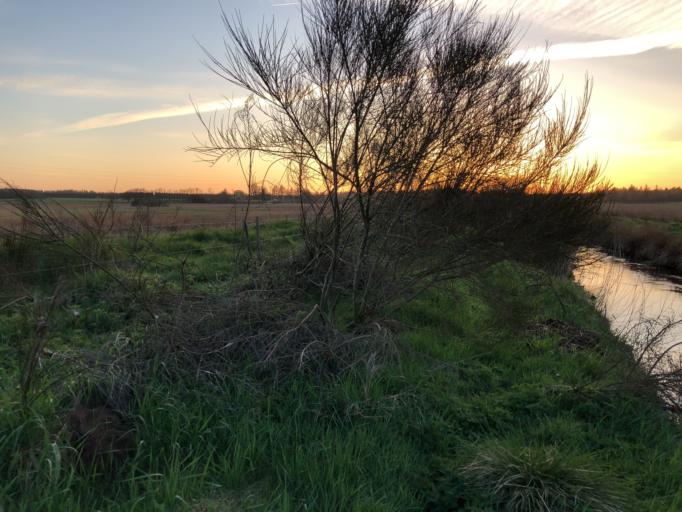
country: DK
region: Central Jutland
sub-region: Holstebro Kommune
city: Ulfborg
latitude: 56.2497
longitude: 8.4043
